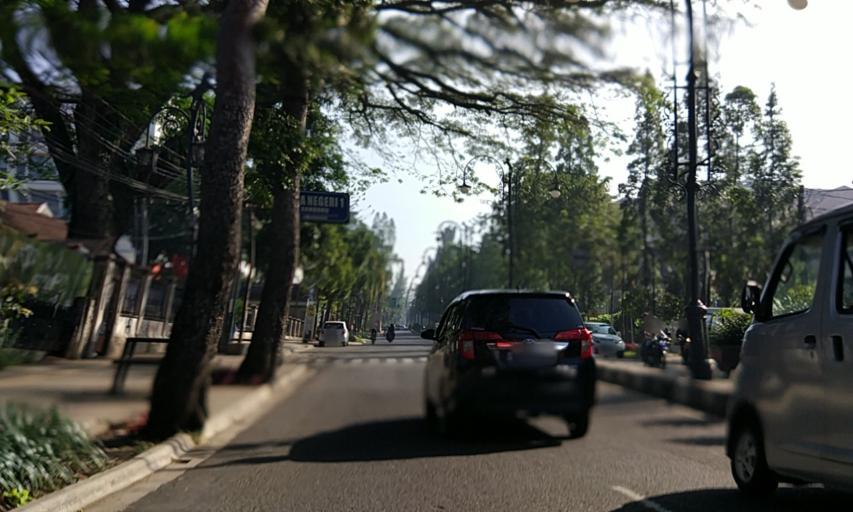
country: ID
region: West Java
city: Bandung
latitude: -6.8959
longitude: 107.6128
